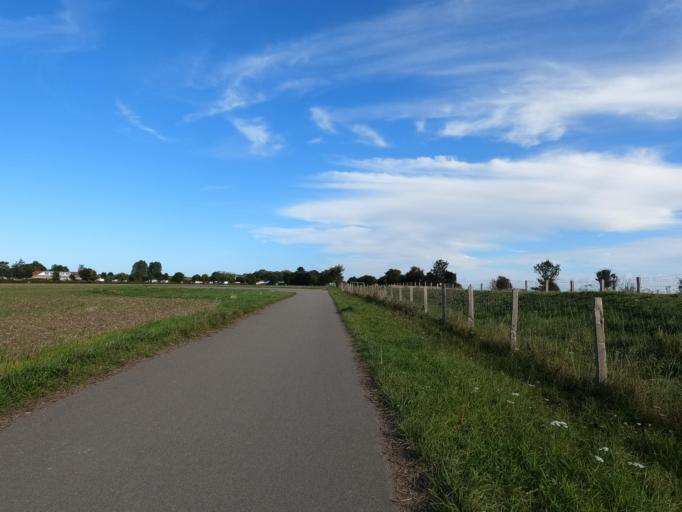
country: DE
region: Schleswig-Holstein
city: Dahme
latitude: 54.2626
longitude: 11.0814
